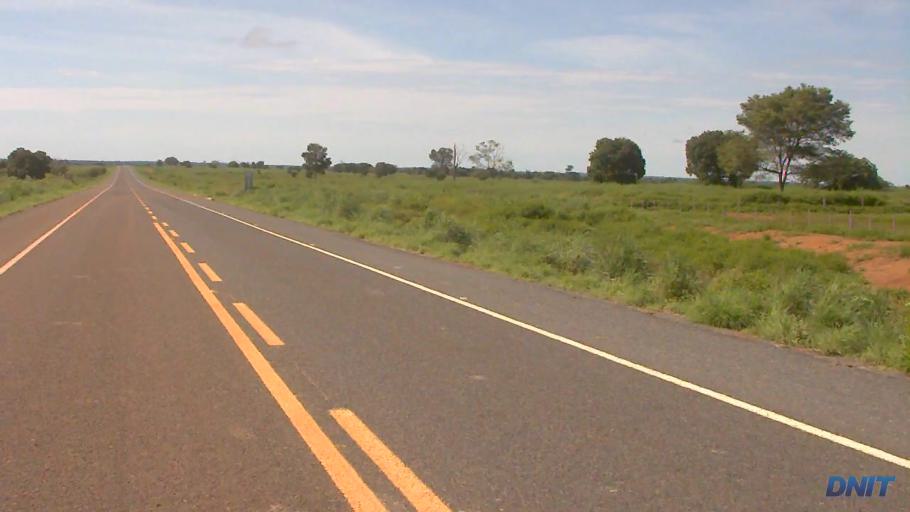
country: BR
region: Goias
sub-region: Sao Miguel Do Araguaia
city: Sao Miguel do Araguaia
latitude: -13.4698
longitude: -50.1151
